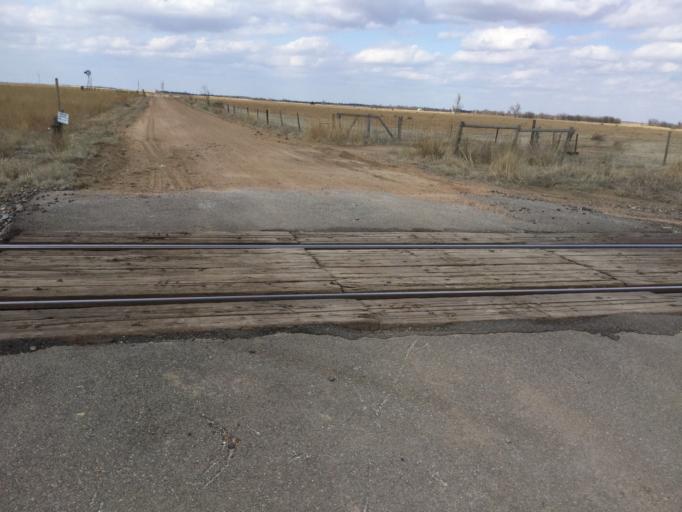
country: US
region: Kansas
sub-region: Kiowa County
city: Greensburg
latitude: 37.6097
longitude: -99.2309
